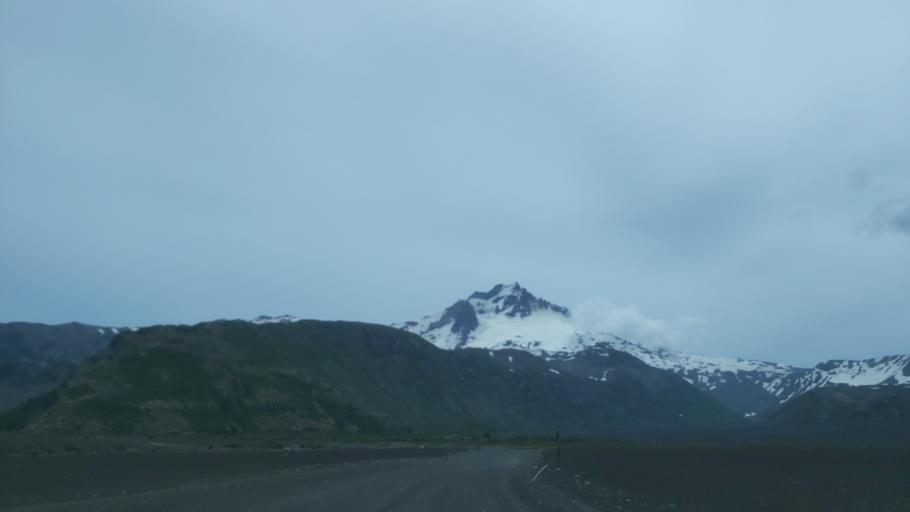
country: AR
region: Neuquen
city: Andacollo
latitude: -37.4613
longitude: -71.3096
